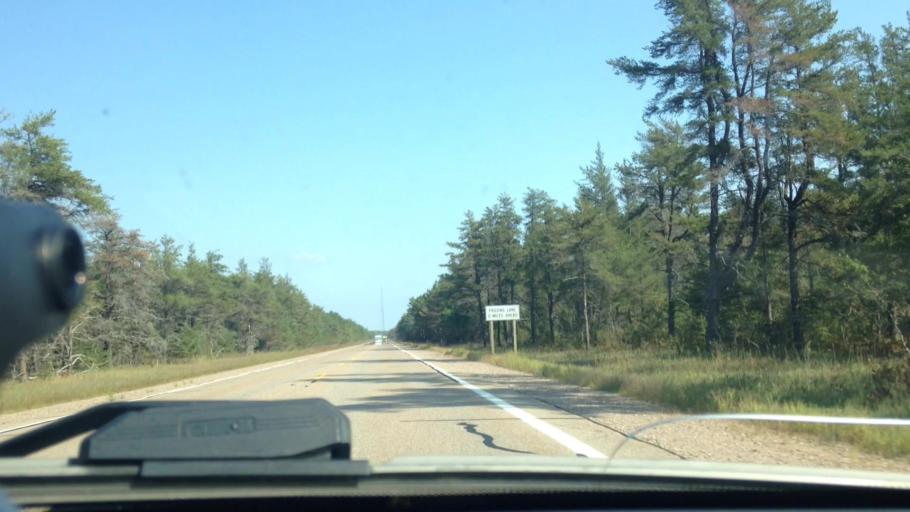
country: US
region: Michigan
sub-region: Chippewa County
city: Sault Ste. Marie
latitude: 46.3587
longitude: -84.8193
